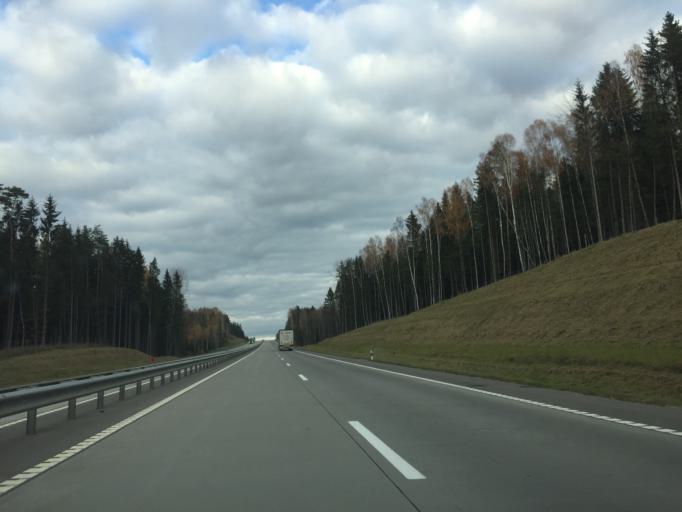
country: BY
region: Minsk
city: Rakaw
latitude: 53.9901
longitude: 27.1101
